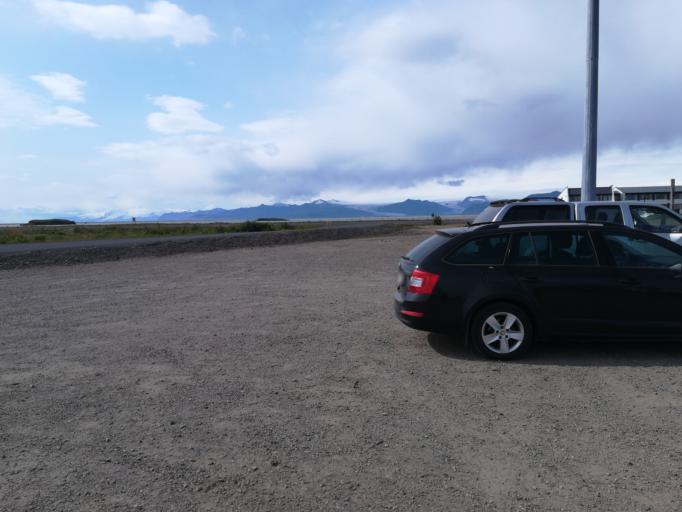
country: IS
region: East
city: Hoefn
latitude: 64.2486
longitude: -15.2047
